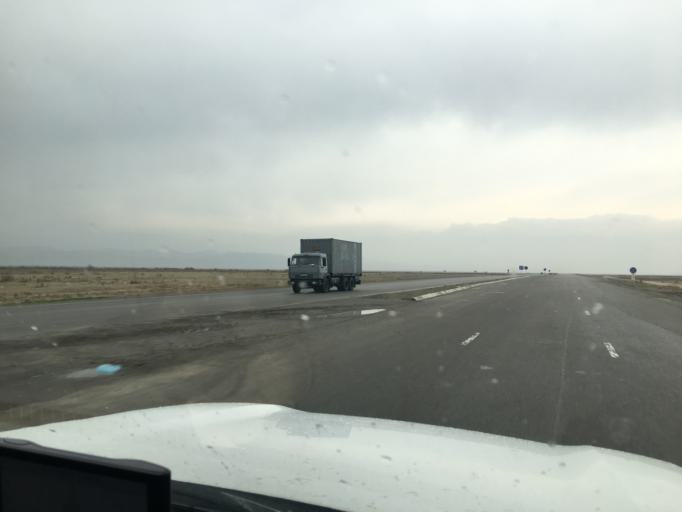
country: IR
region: Razavi Khorasan
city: Dargaz
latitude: 37.5805
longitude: 59.3133
